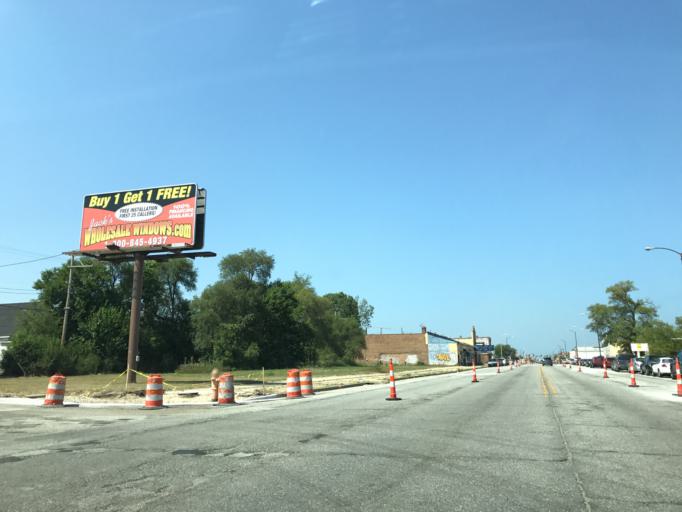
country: US
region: Indiana
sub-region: Lake County
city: Gary
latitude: 41.5767
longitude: -87.3368
